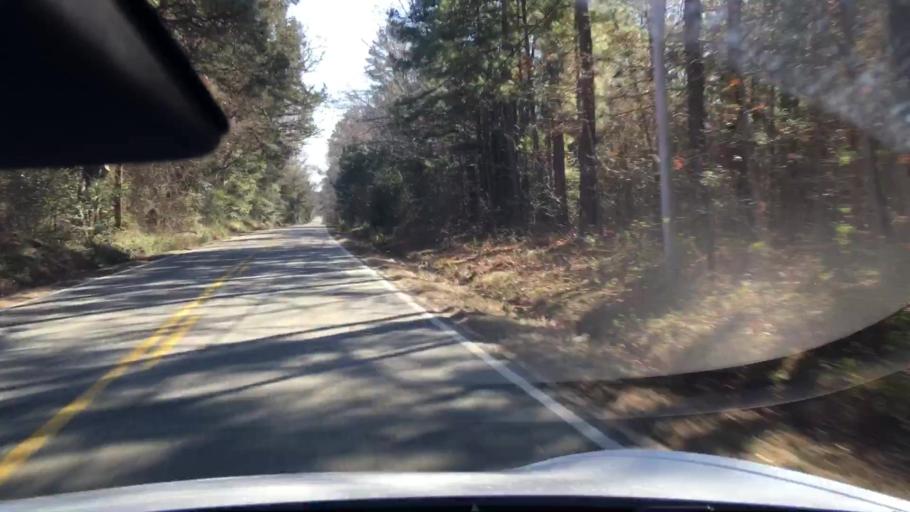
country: US
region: Virginia
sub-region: Henrico County
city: Short Pump
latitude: 37.5841
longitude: -77.7465
